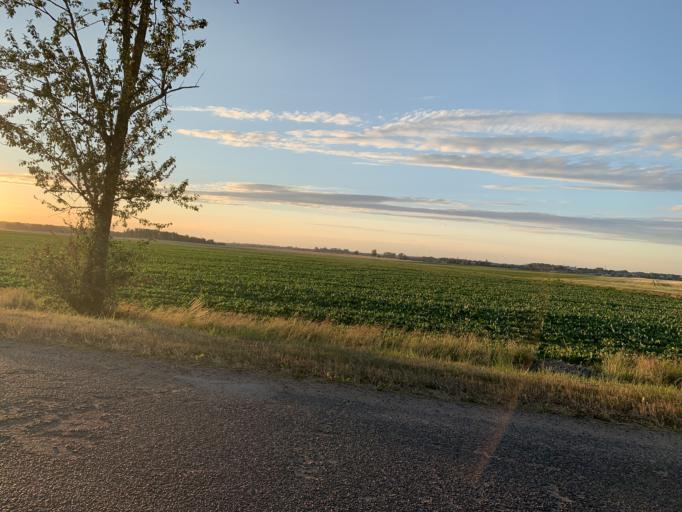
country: BY
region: Minsk
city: Nyasvizh
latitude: 53.1904
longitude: 26.6829
